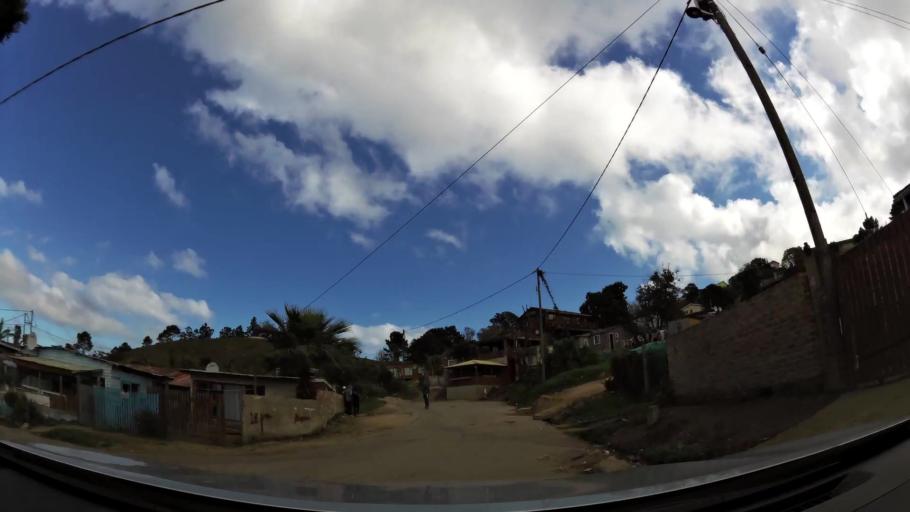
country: ZA
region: Western Cape
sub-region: Eden District Municipality
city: Knysna
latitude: -34.0498
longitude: 23.0906
